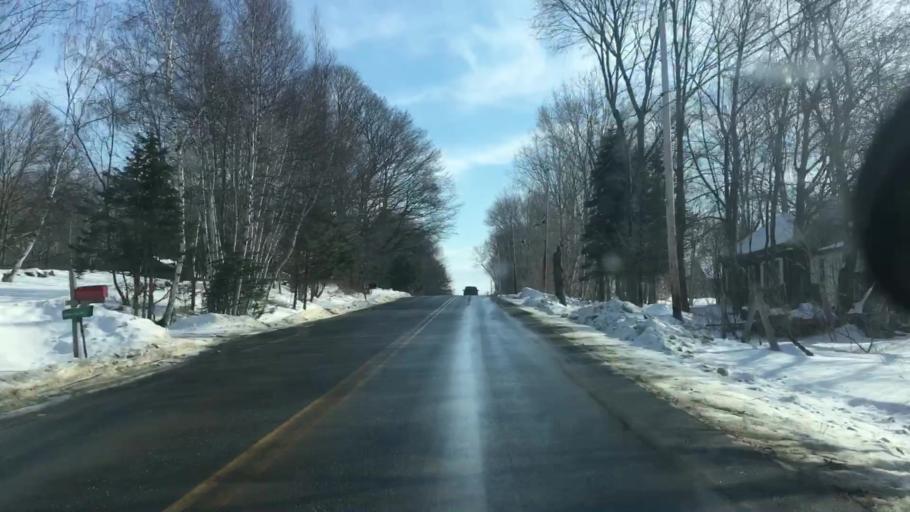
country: US
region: Maine
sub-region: Penobscot County
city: Bangor
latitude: 44.8493
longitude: -68.8408
